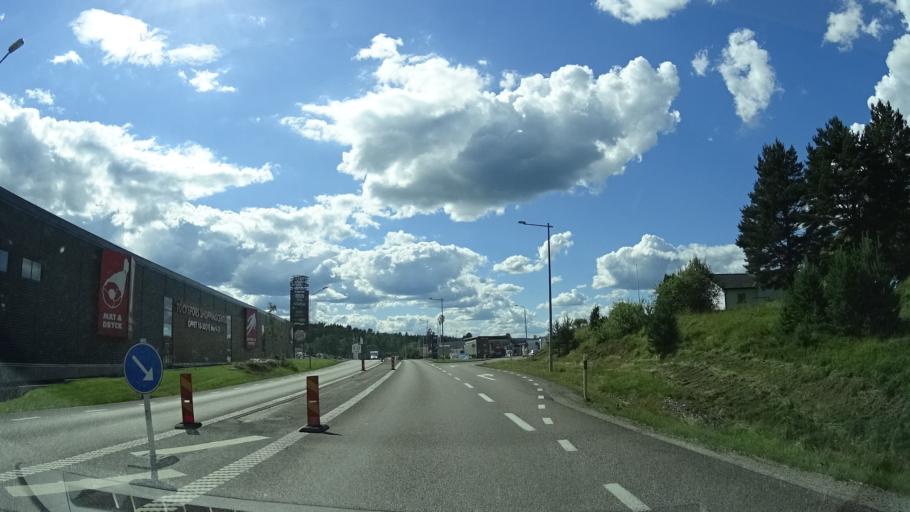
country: SE
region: Vaermland
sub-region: Arjangs Kommun
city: Toecksfors
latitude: 59.5077
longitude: 11.8467
